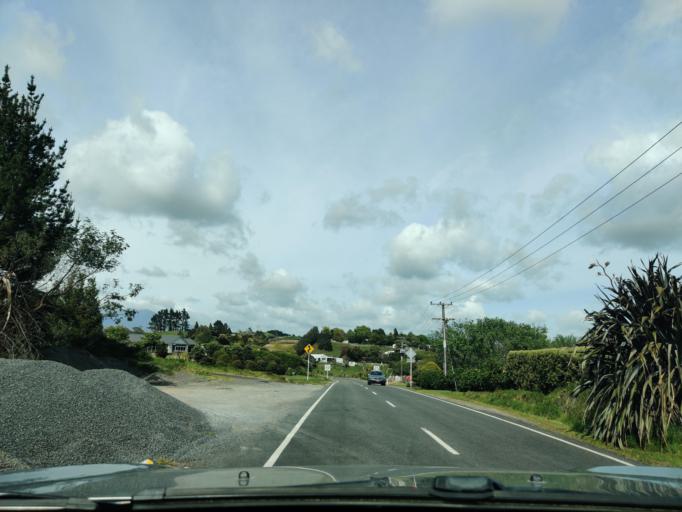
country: NZ
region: Taranaki
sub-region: New Plymouth District
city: New Plymouth
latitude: -39.0938
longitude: 174.1048
